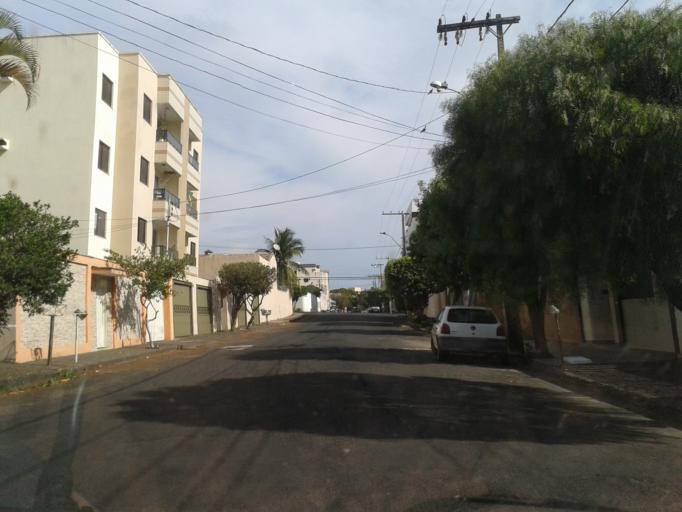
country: BR
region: Minas Gerais
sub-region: Uberlandia
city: Uberlandia
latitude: -18.9187
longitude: -48.2522
